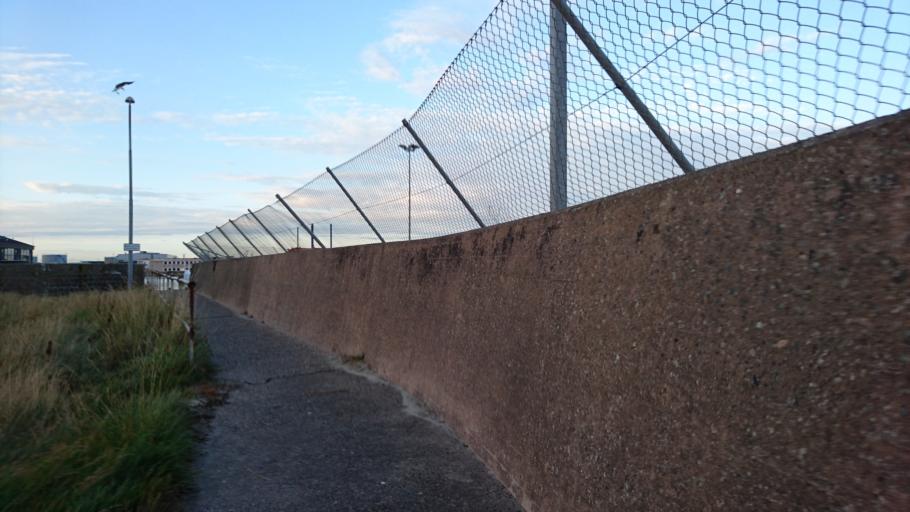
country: DK
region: North Denmark
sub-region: Frederikshavn Kommune
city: Skagen
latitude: 57.7153
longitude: 10.5895
